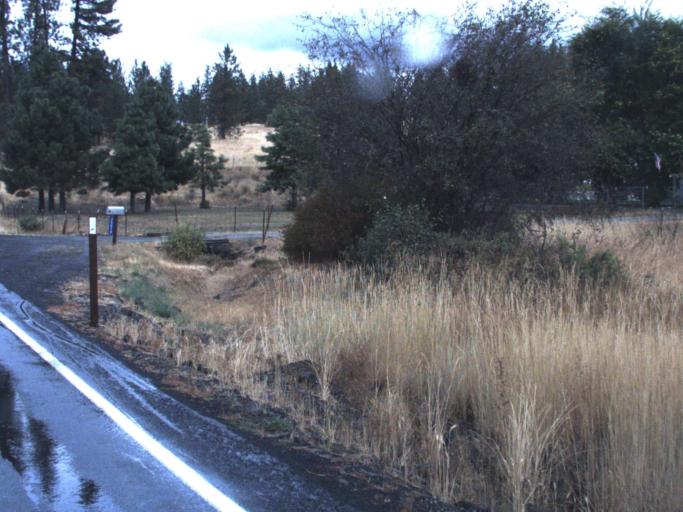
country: US
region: Washington
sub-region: Lincoln County
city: Davenport
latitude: 47.7826
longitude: -117.8889
